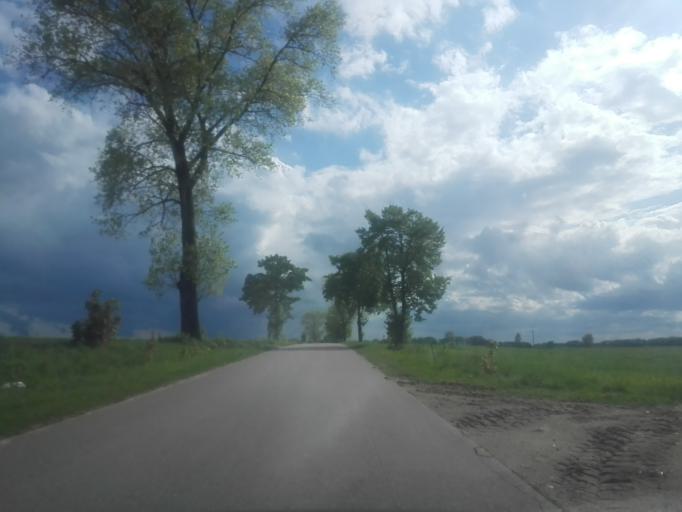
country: PL
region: Podlasie
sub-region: Powiat lomzynski
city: Wizna
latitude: 53.2359
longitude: 22.4284
